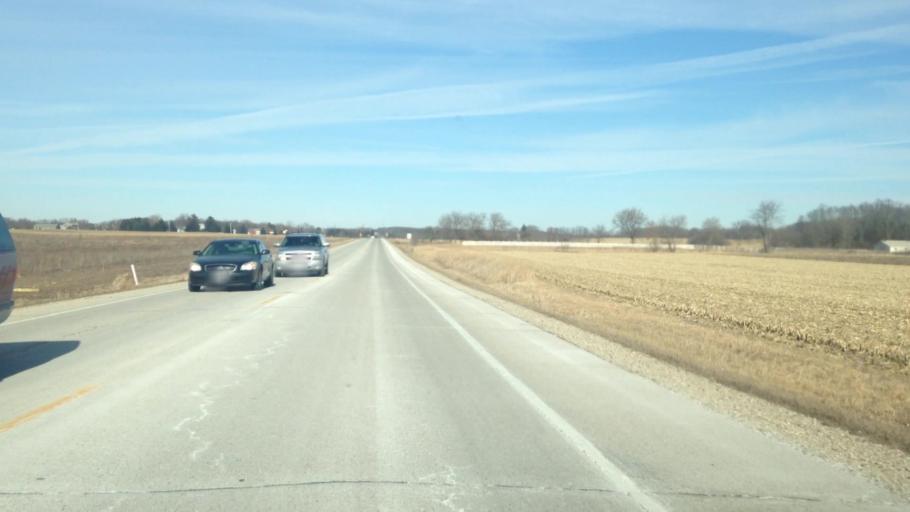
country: US
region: Wisconsin
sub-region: Washington County
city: Slinger
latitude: 43.2734
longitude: -88.2614
